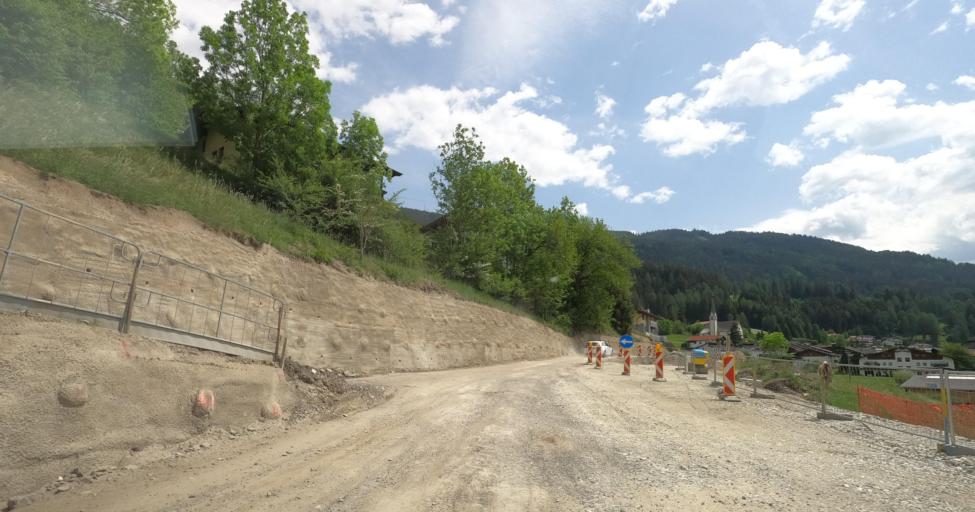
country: AT
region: Tyrol
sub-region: Politischer Bezirk Innsbruck Land
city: Pfons
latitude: 47.1444
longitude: 11.4585
